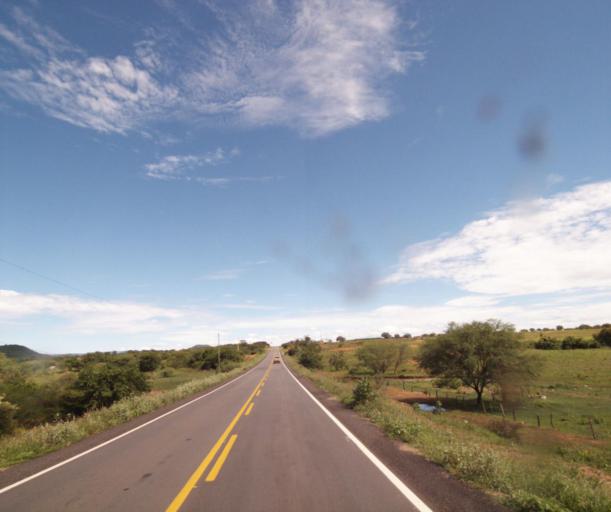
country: BR
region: Bahia
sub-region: Guanambi
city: Guanambi
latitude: -14.3777
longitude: -42.7721
